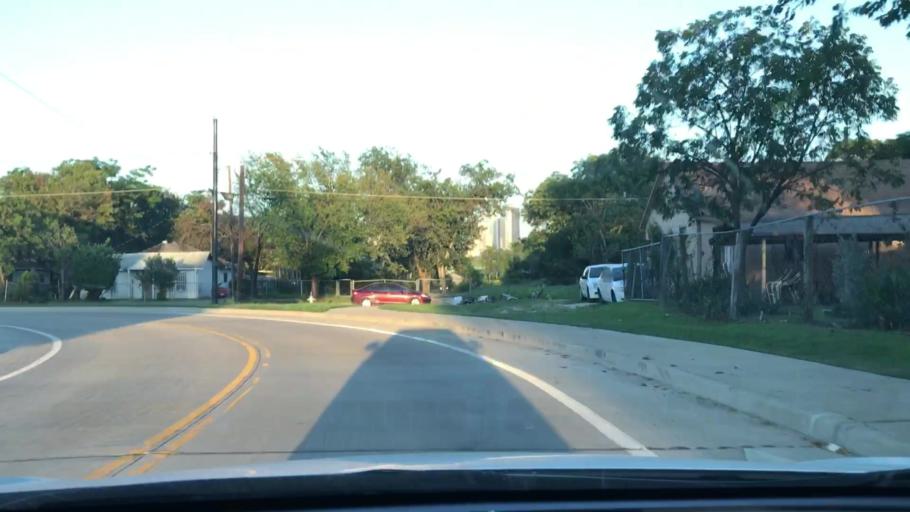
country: US
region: Texas
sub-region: Dallas County
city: Dallas
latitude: 32.7838
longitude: -96.8353
